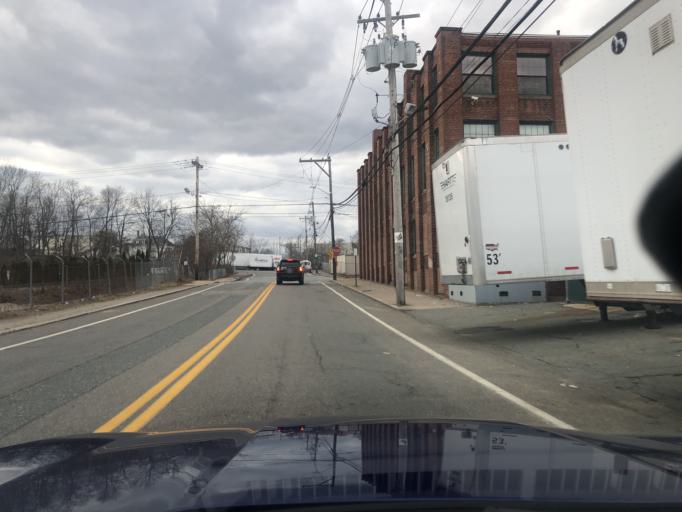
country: US
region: Massachusetts
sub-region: Plymouth County
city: Brockton
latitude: 42.1065
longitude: -71.0198
